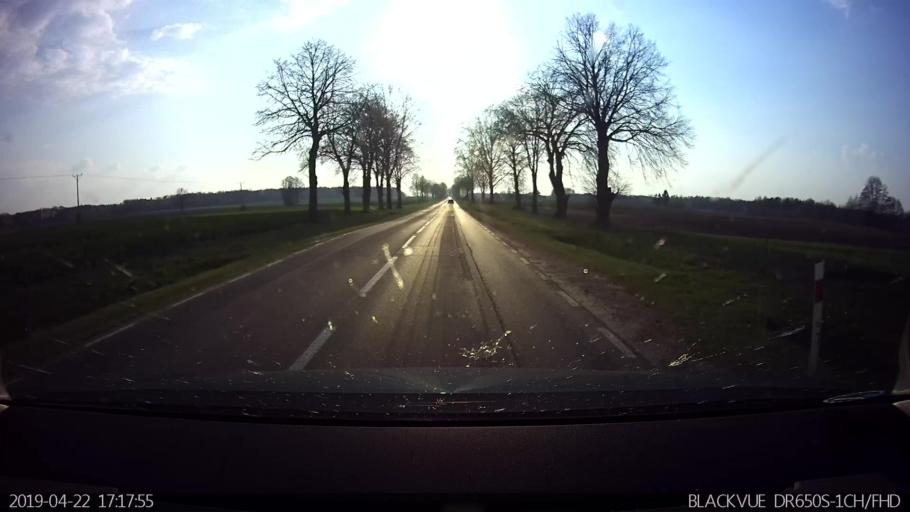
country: PL
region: Masovian Voivodeship
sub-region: Powiat sokolowski
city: Repki
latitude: 52.3857
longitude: 22.4273
